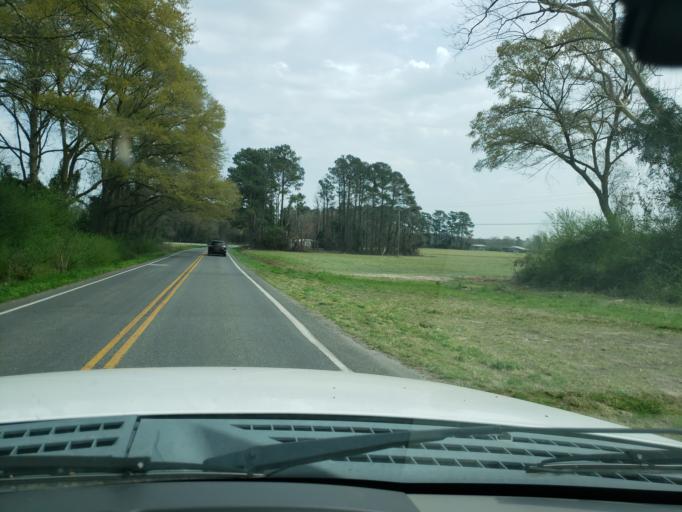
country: US
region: North Carolina
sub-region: Duplin County
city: Beulaville
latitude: 34.7785
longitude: -77.8277
